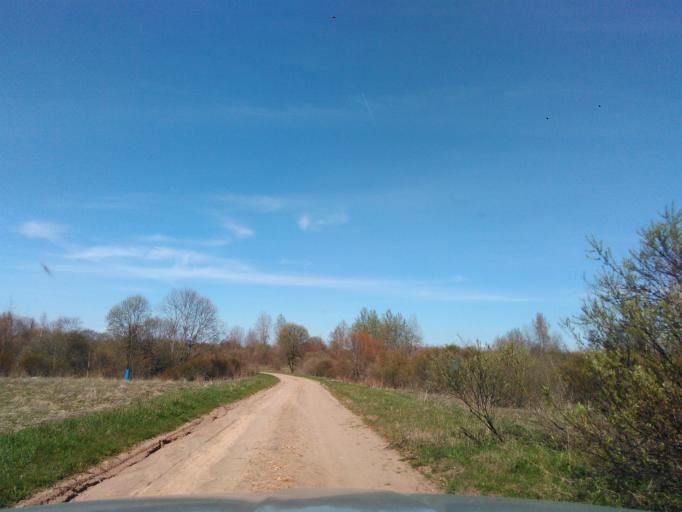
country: BY
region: Vitebsk
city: Konstantinovo
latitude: 54.6792
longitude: 29.4794
